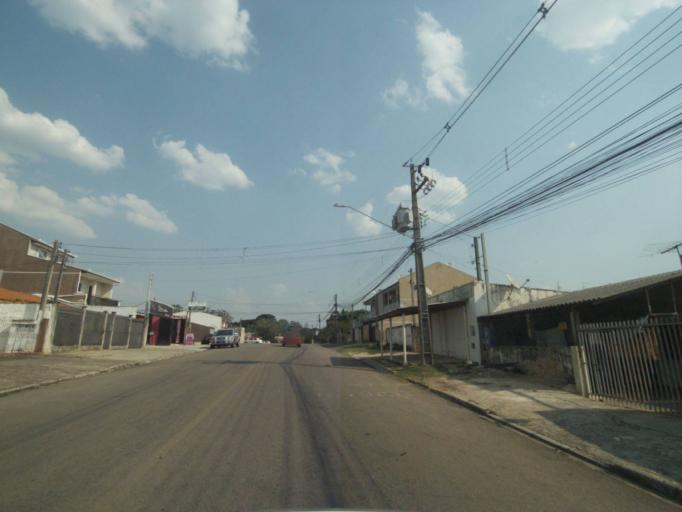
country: BR
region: Parana
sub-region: Sao Jose Dos Pinhais
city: Sao Jose dos Pinhais
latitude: -25.5401
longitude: -49.2405
